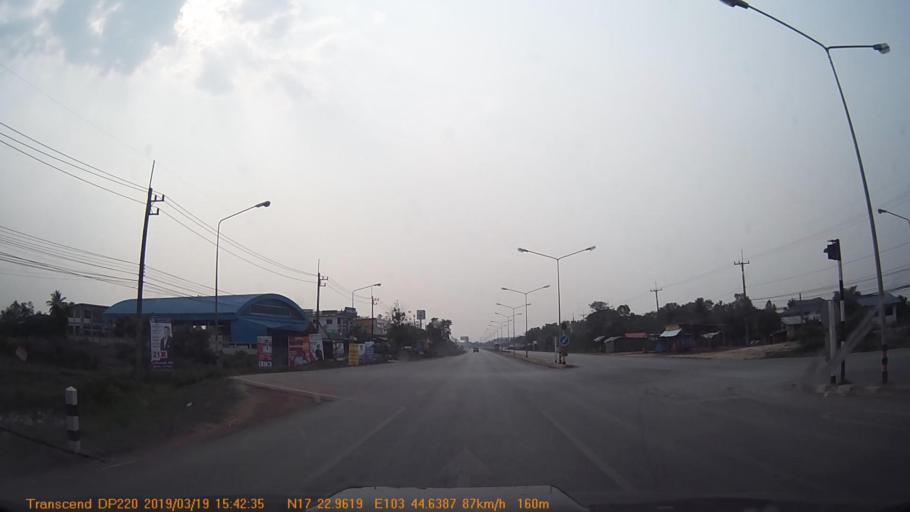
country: TH
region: Sakon Nakhon
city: Phang Khon
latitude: 17.3828
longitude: 103.7437
